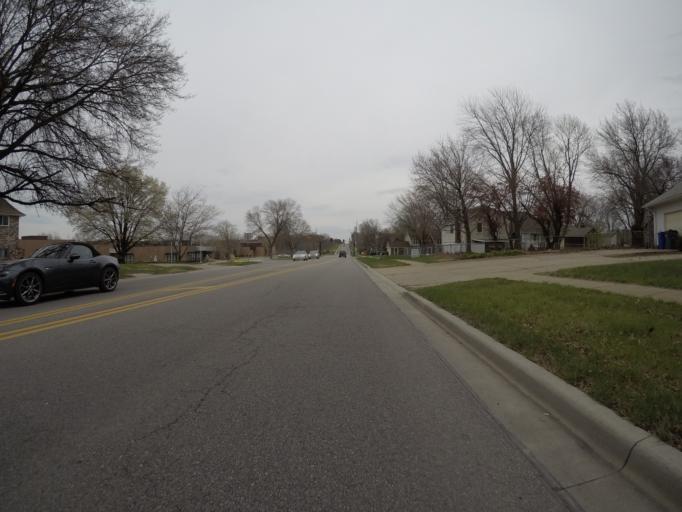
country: US
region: Kansas
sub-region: Johnson County
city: Olathe
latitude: 38.8691
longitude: -94.7892
